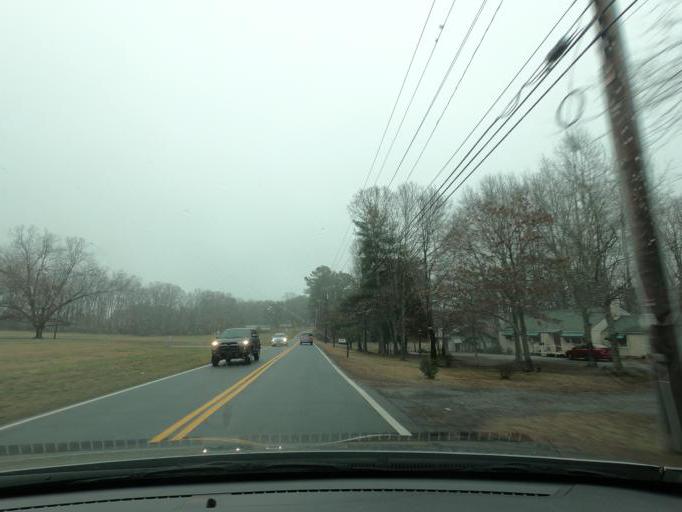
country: US
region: Georgia
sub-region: Fulton County
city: Alpharetta
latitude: 34.0938
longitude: -84.3322
